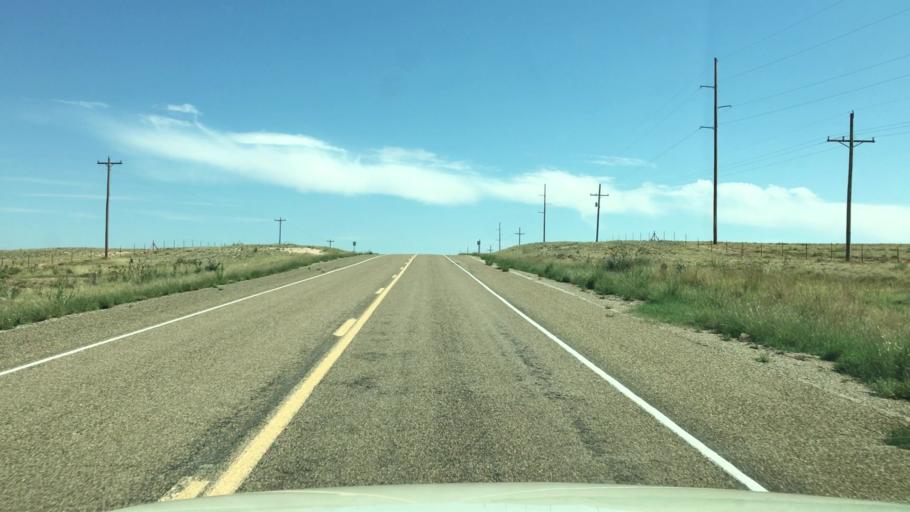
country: US
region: New Mexico
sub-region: Chaves County
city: Roswell
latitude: 33.9361
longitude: -104.5946
